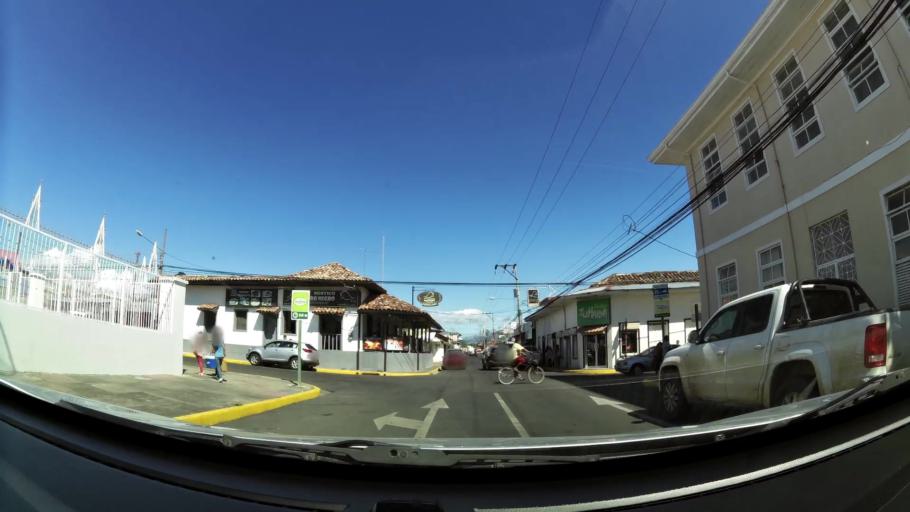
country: CR
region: Guanacaste
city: Liberia
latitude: 10.6298
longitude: -85.4371
